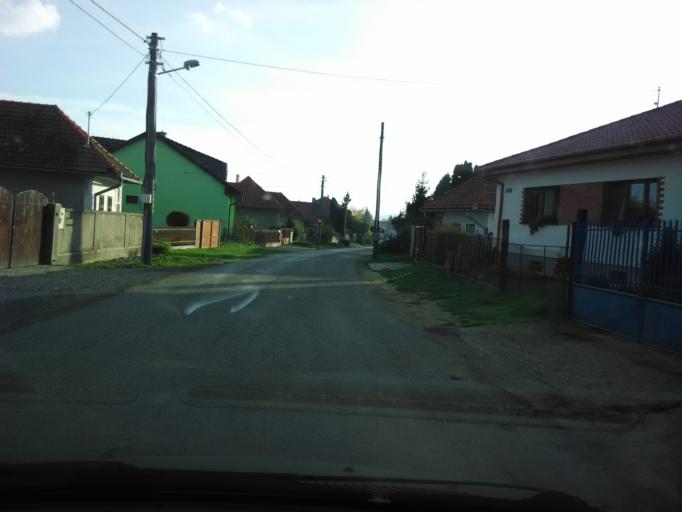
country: SK
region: Nitriansky
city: Tlmace
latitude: 48.3166
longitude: 18.5188
